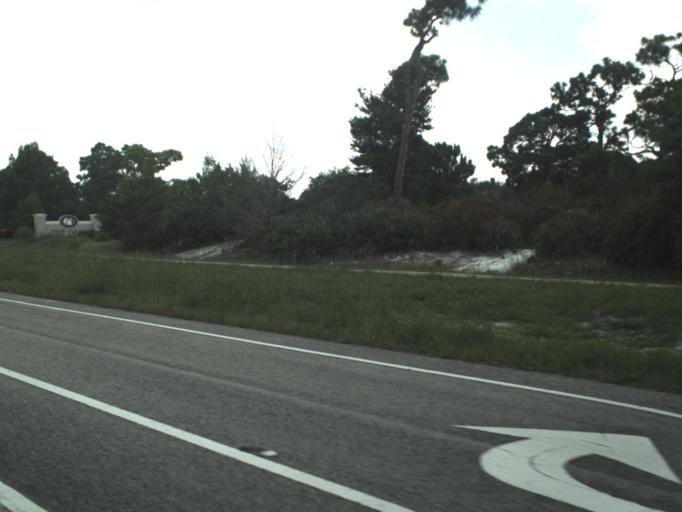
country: US
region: Florida
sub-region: Martin County
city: Port Salerno
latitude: 27.1090
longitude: -80.1696
